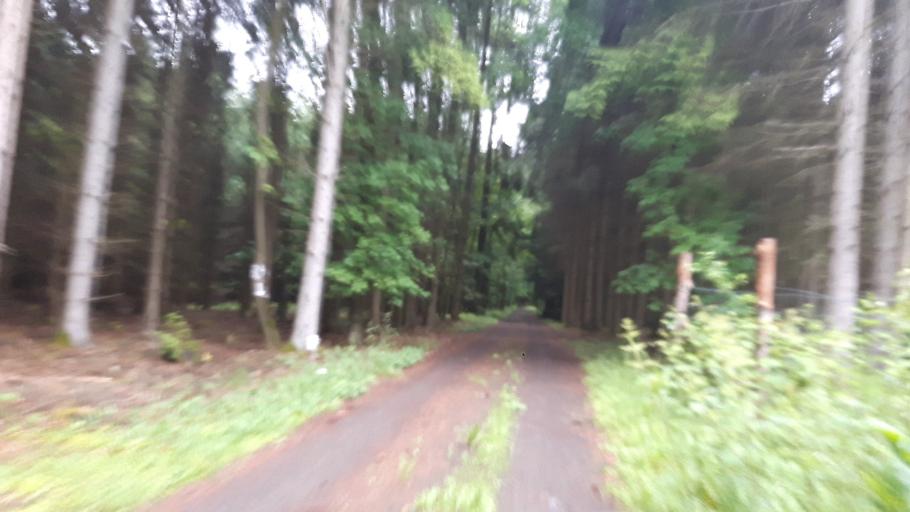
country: DE
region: Bavaria
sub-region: Regierungsbezirk Unterfranken
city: Stadtlauringen
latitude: 50.1271
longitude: 10.3298
